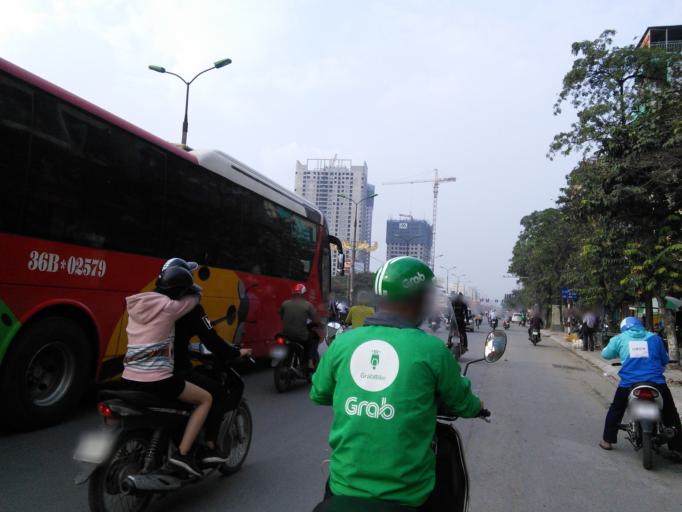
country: VN
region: Ha Noi
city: Hai BaTrung
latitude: 20.9818
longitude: 105.8412
